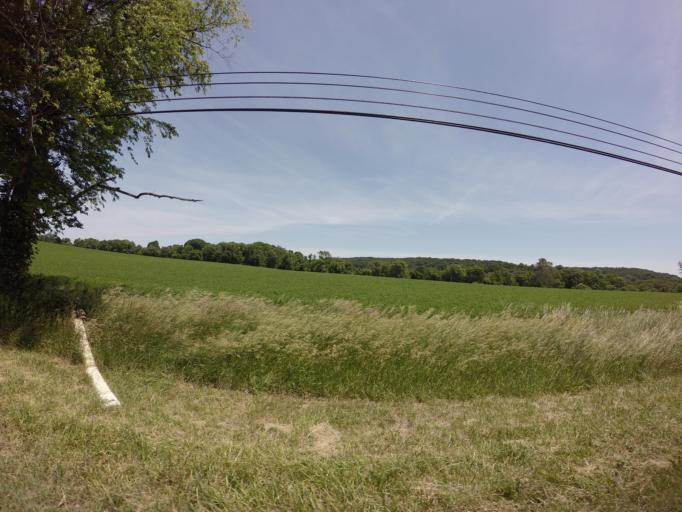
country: US
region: Maryland
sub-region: Frederick County
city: Bartonsville
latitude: 39.3728
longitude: -77.3937
